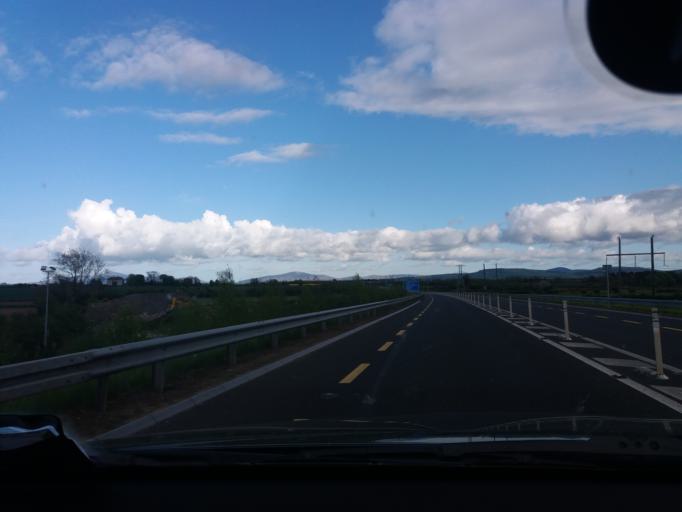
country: IE
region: Leinster
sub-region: Kilkenny
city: Kilkenny
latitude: 52.6385
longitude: -7.1652
